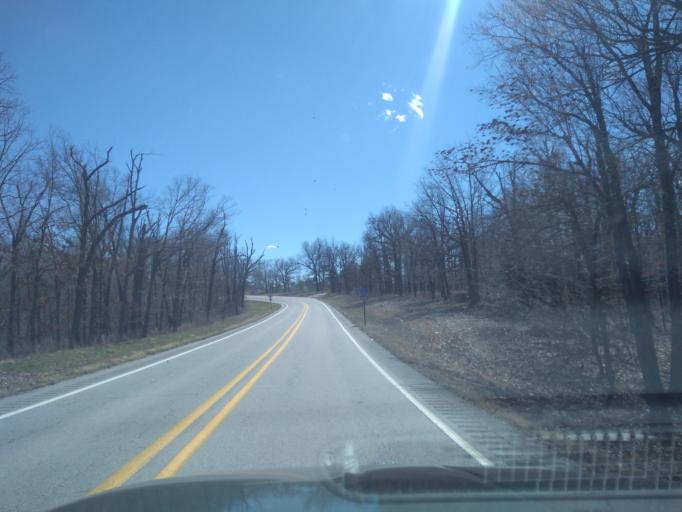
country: US
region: Arkansas
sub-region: Washington County
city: Farmington
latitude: 36.0819
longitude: -94.3201
